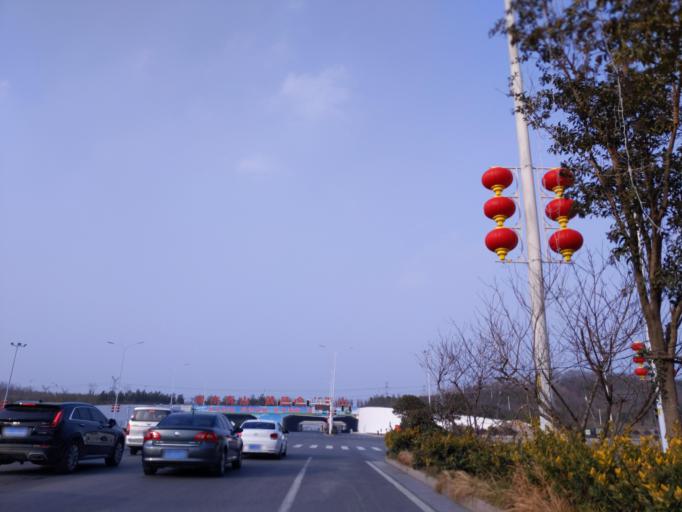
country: CN
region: Henan Sheng
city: Puyang
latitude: 35.8166
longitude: 115.0226
